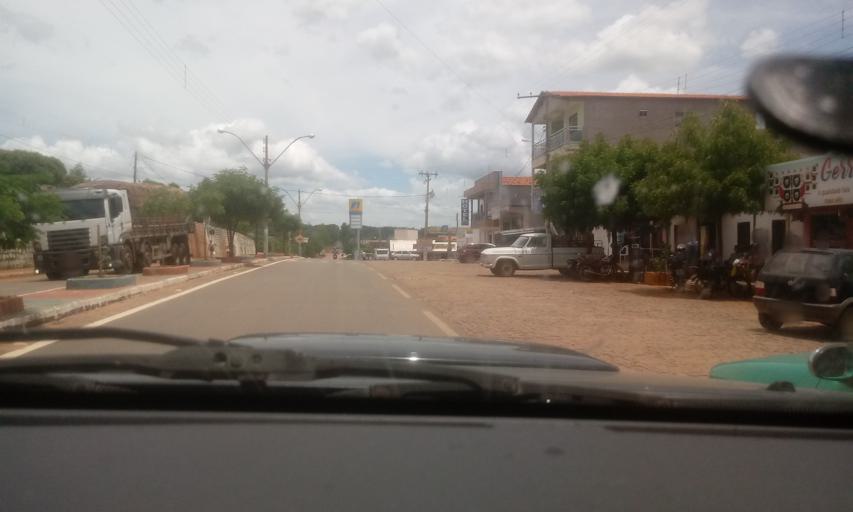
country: BR
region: Bahia
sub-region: Riacho De Santana
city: Riacho de Santana
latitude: -13.6061
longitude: -42.9366
